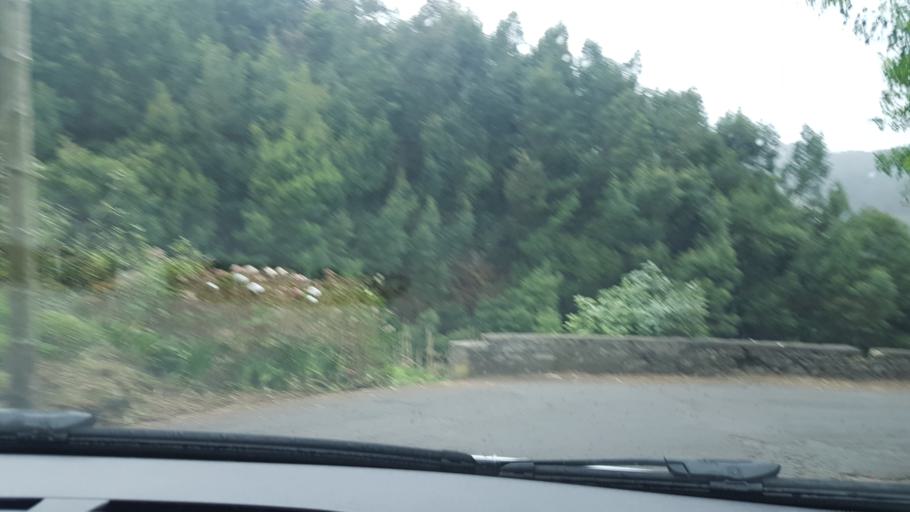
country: PT
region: Madeira
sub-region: Santa Cruz
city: Santa Cruz
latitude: 32.7293
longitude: -16.8090
